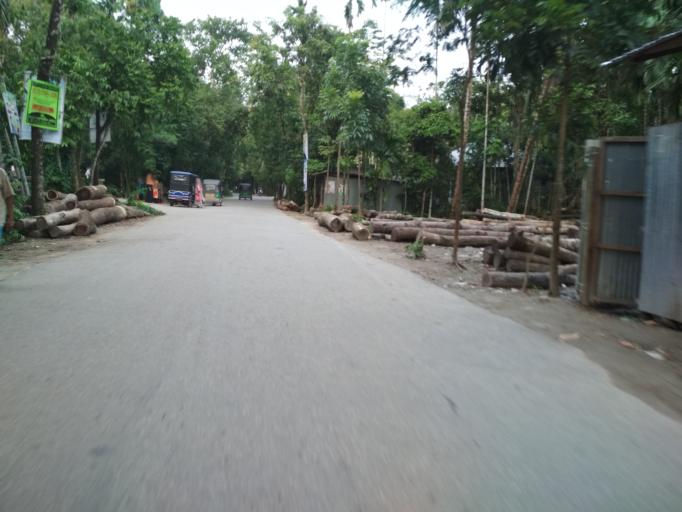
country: BD
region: Chittagong
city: Raipur
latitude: 23.0062
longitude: 90.7079
